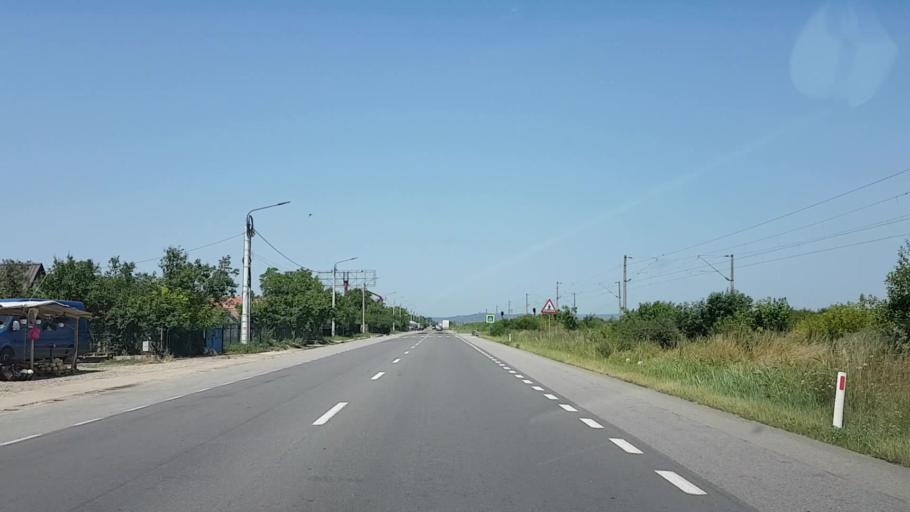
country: RO
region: Cluj
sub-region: Comuna Apahida
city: Apahida
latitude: 46.8431
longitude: 23.7505
